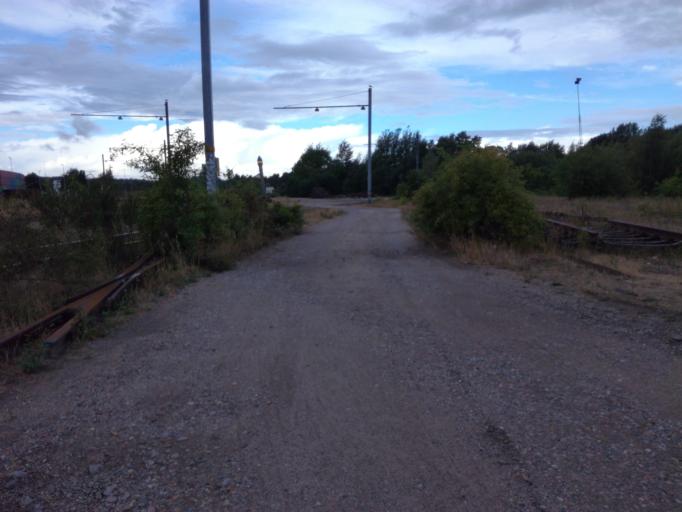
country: DK
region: South Denmark
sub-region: Fredericia Kommune
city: Fredericia
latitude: 55.5626
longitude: 9.7437
